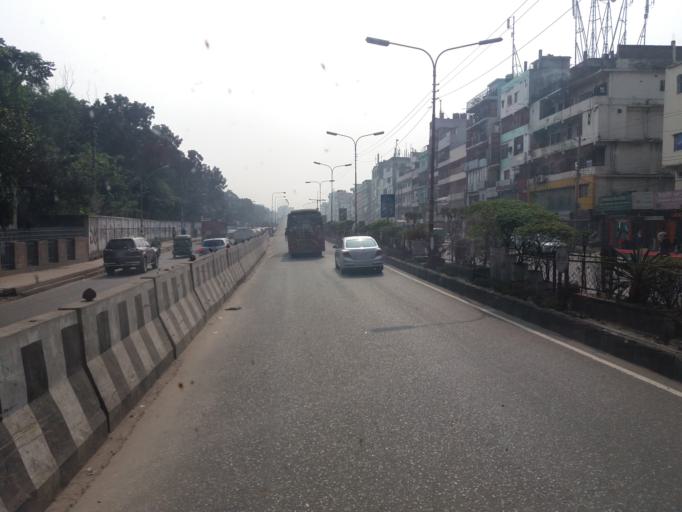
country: BD
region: Dhaka
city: Paltan
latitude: 23.7843
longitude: 90.3993
